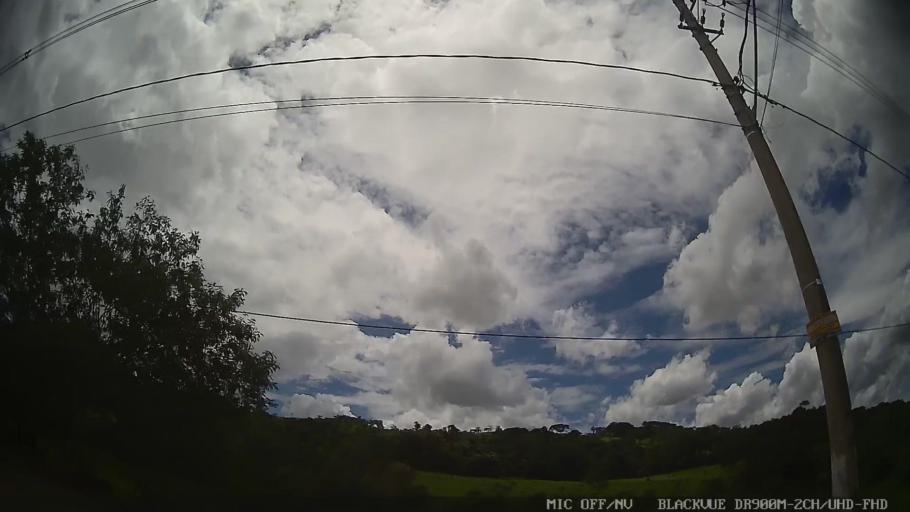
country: BR
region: Sao Paulo
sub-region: Jaguariuna
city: Jaguariuna
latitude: -22.6974
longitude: -46.9603
